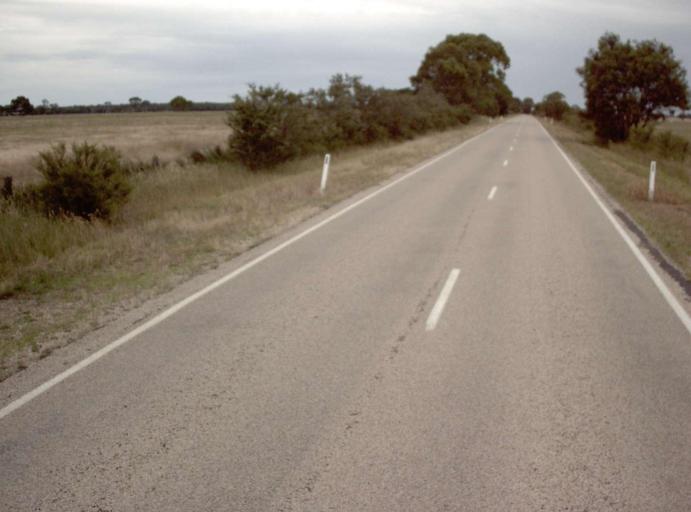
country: AU
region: Victoria
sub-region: East Gippsland
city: Bairnsdale
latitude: -37.8859
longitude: 147.5577
